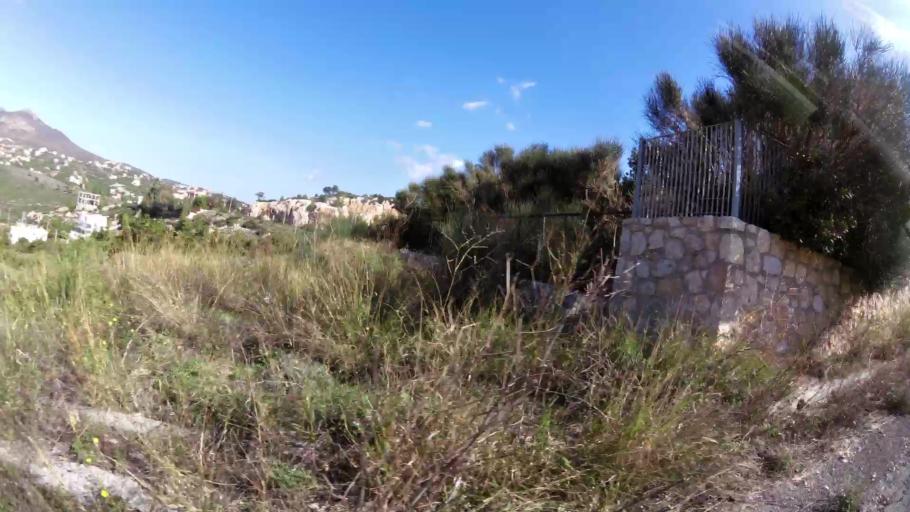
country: GR
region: Attica
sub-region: Nomarchia Anatolikis Attikis
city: Dhrafi
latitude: 38.0180
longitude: 23.9181
